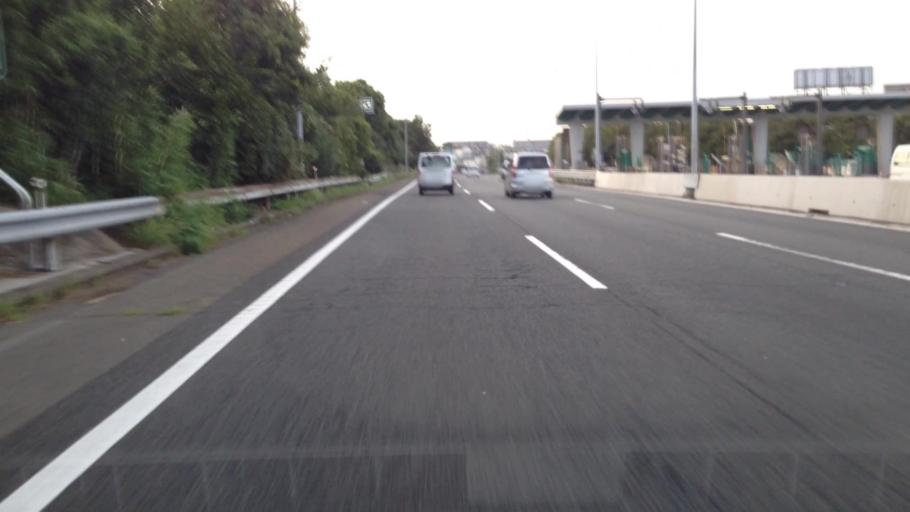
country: JP
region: Kanagawa
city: Yokohama
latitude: 35.4833
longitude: 139.5938
